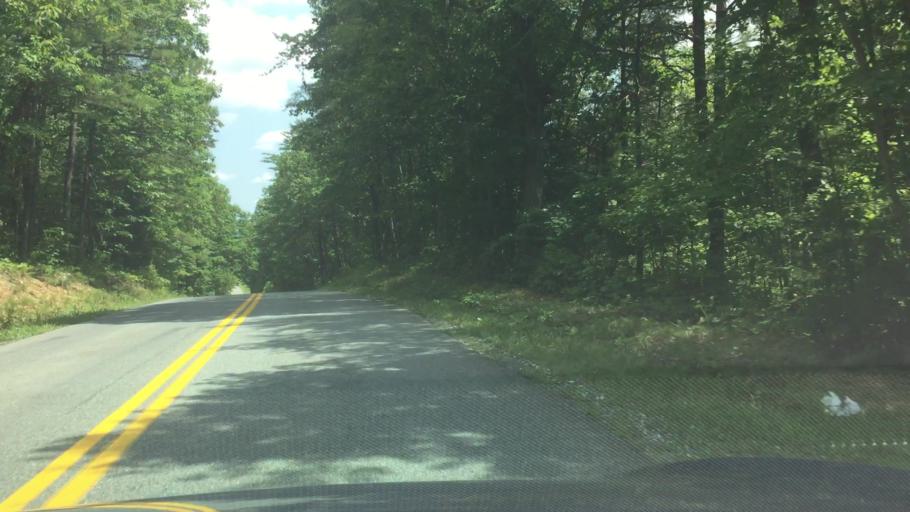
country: US
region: Virginia
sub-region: Appomattox County
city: Appomattox
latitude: 37.3182
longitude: -78.8476
